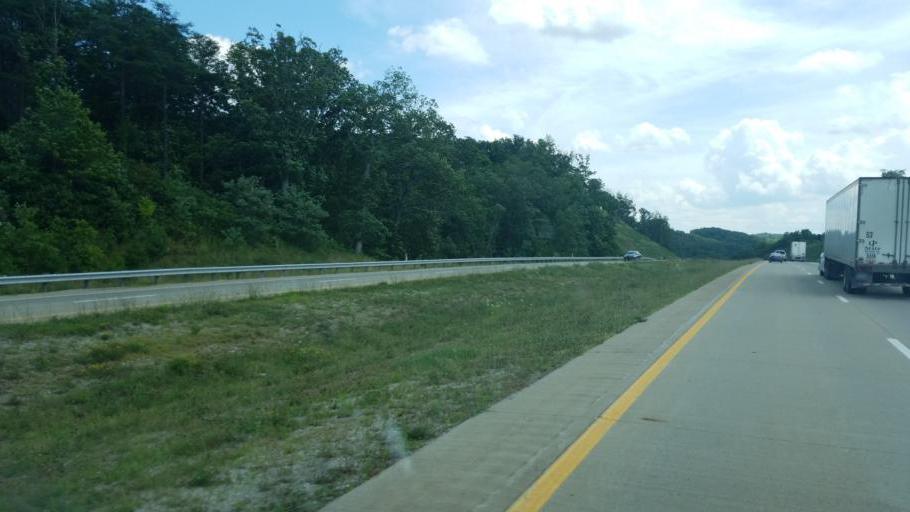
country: US
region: West Virginia
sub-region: Mason County
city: Point Pleasant
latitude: 38.7745
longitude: -82.0576
